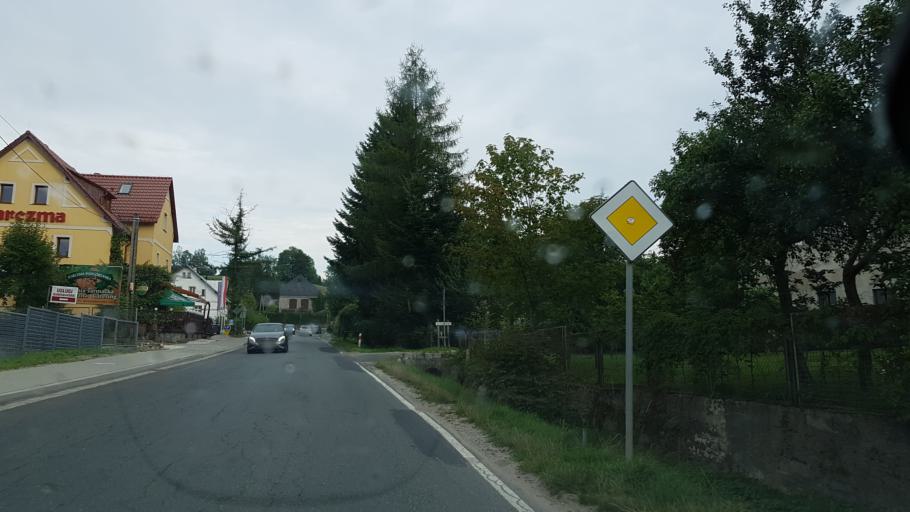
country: PL
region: Lower Silesian Voivodeship
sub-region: Powiat jeleniogorski
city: Janowice Wielkie
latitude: 50.9077
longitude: 15.9594
